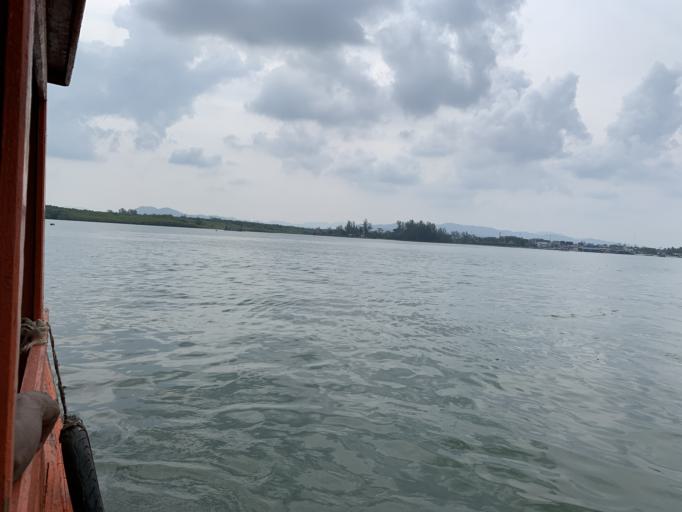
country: TH
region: Phangnga
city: Takua Pa
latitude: 8.8805
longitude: 98.2725
